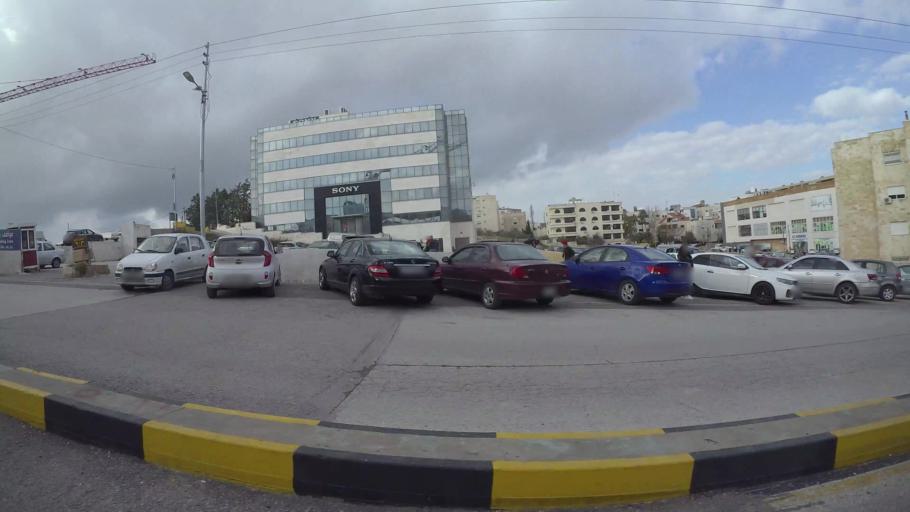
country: JO
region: Amman
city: Wadi as Sir
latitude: 31.9778
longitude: 35.8425
